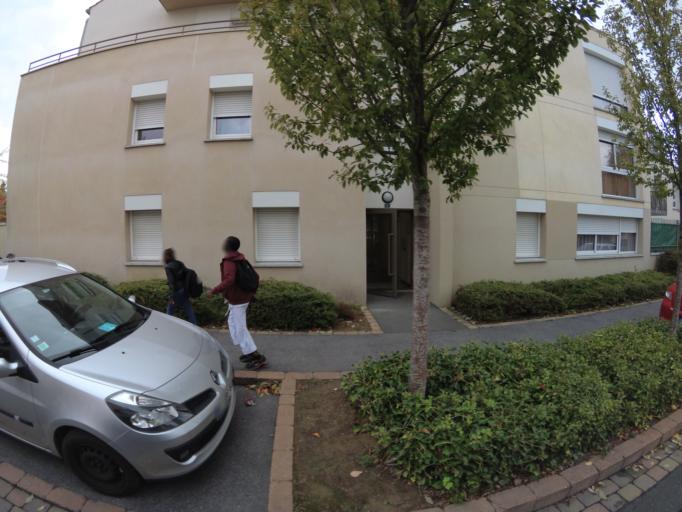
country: FR
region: Ile-de-France
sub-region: Departement de Seine-et-Marne
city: Chessy
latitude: 48.8795
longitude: 2.7720
